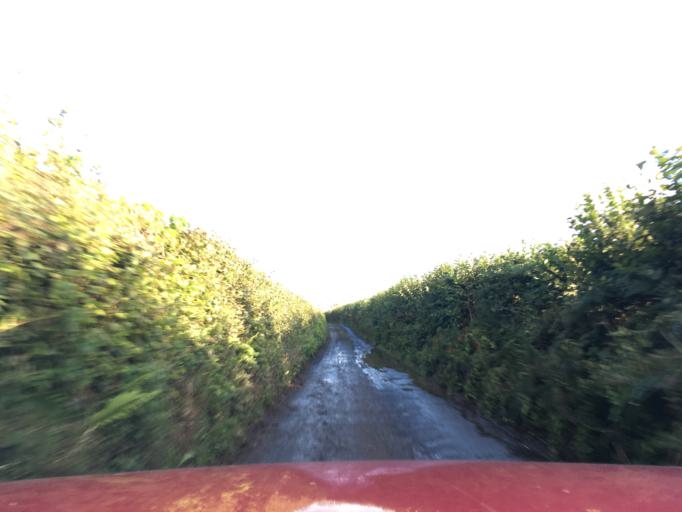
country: GB
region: England
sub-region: Devon
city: Dartmouth
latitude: 50.3445
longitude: -3.6104
